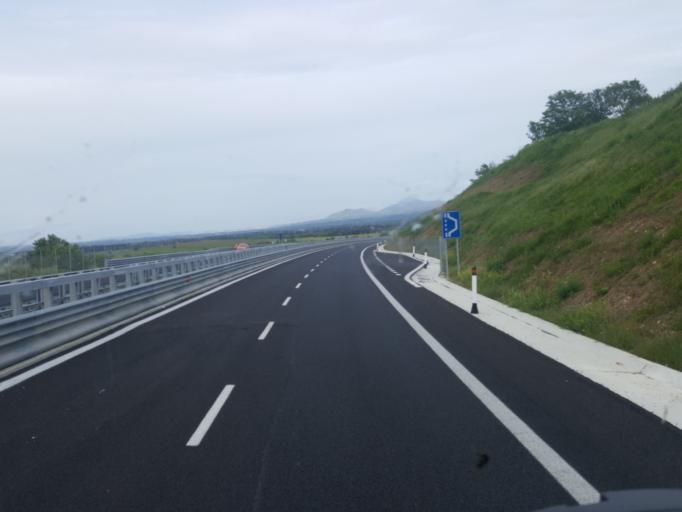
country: IT
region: Latium
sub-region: Provincia di Viterbo
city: Monte Romano
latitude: 42.2943
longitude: 11.9442
